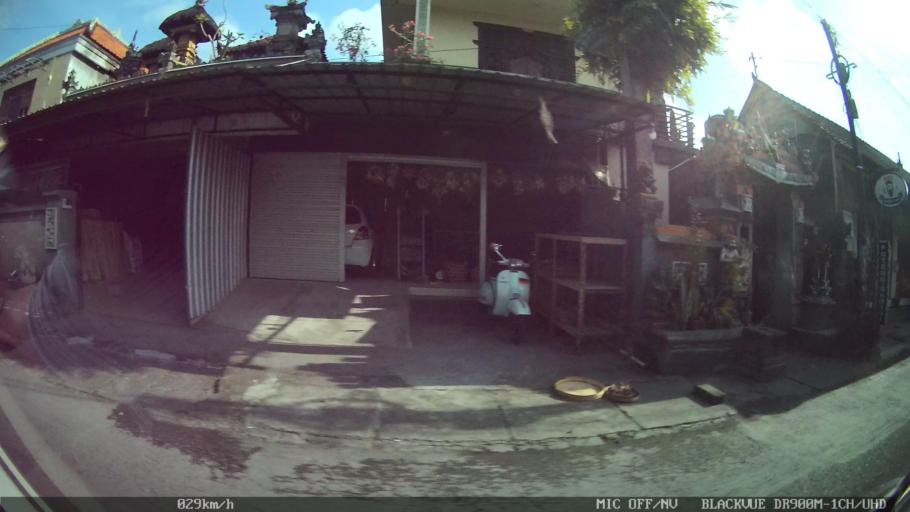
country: ID
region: Bali
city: Banjar Pekenjelodan
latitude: -8.5701
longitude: 115.1848
